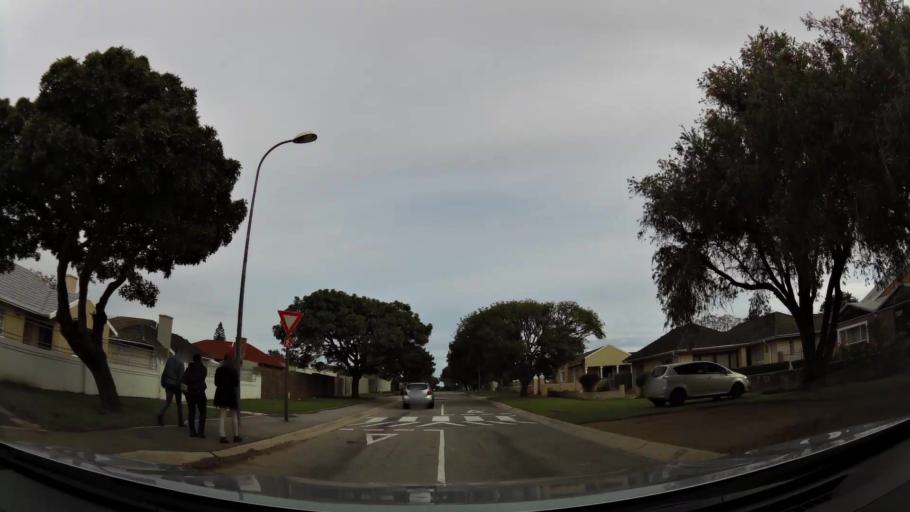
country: ZA
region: Eastern Cape
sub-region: Nelson Mandela Bay Metropolitan Municipality
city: Port Elizabeth
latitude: -33.9428
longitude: 25.5009
